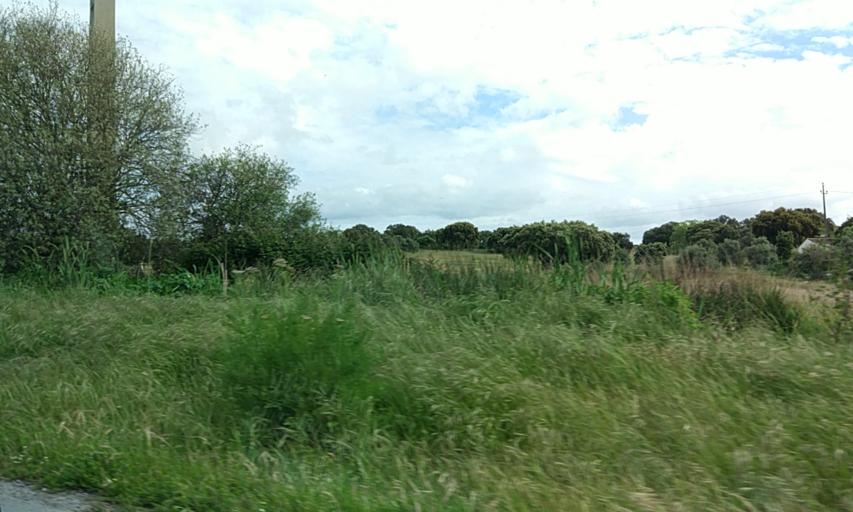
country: PT
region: Evora
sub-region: Evora
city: Evora
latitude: 38.5675
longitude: -7.9397
